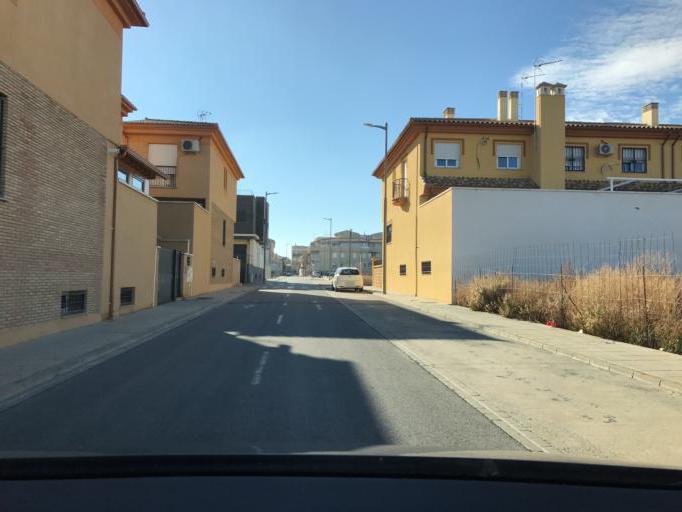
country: ES
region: Andalusia
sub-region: Provincia de Granada
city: Churriana de la Vega
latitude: 37.1503
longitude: -3.6505
